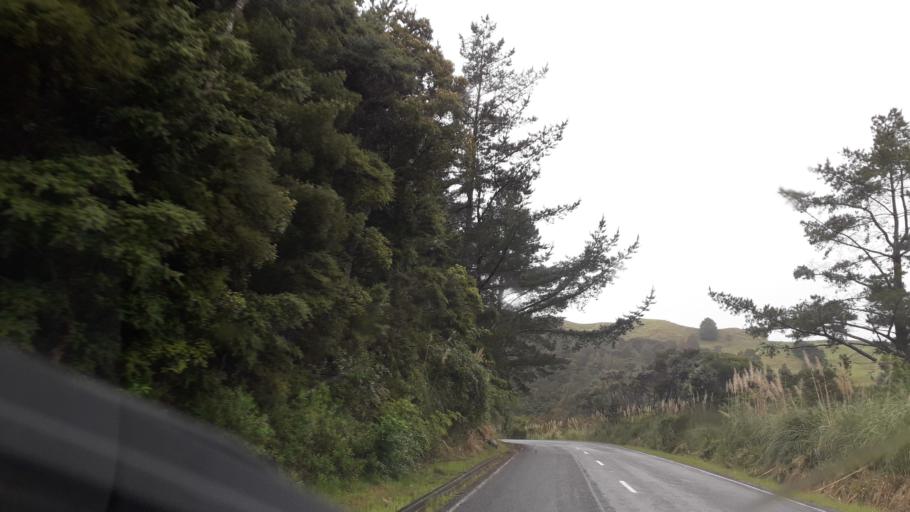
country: NZ
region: Northland
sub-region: Far North District
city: Kaitaia
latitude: -35.3631
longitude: 173.4713
